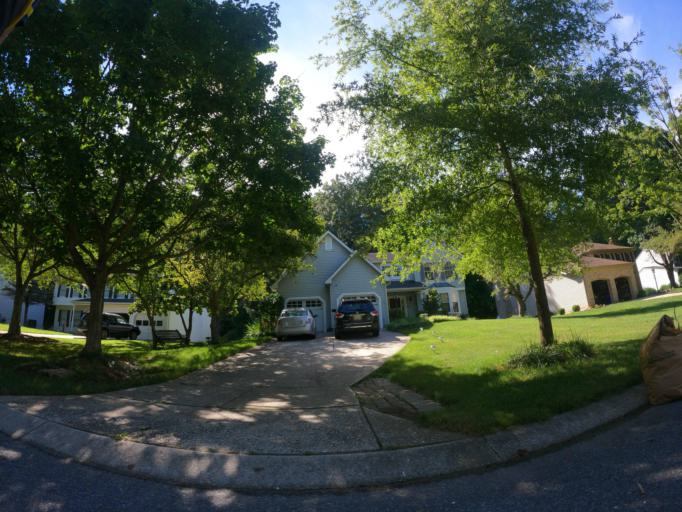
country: US
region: Maryland
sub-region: Howard County
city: Savage
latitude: 39.1486
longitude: -76.8389
